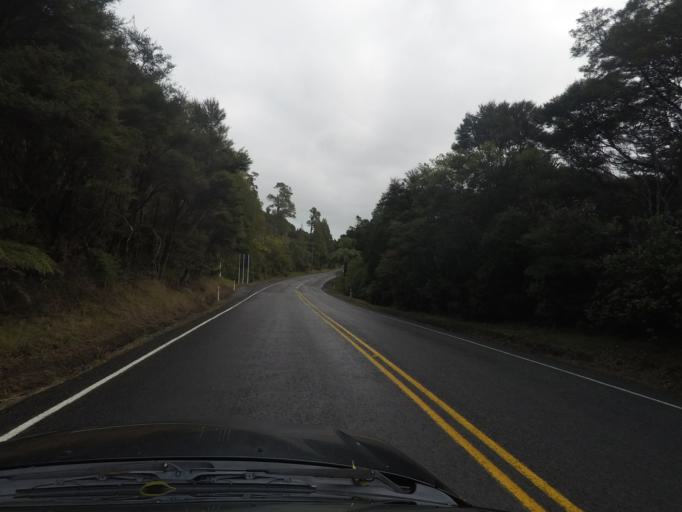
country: NZ
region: Auckland
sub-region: Auckland
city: Muriwai Beach
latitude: -36.8782
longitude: 174.5412
